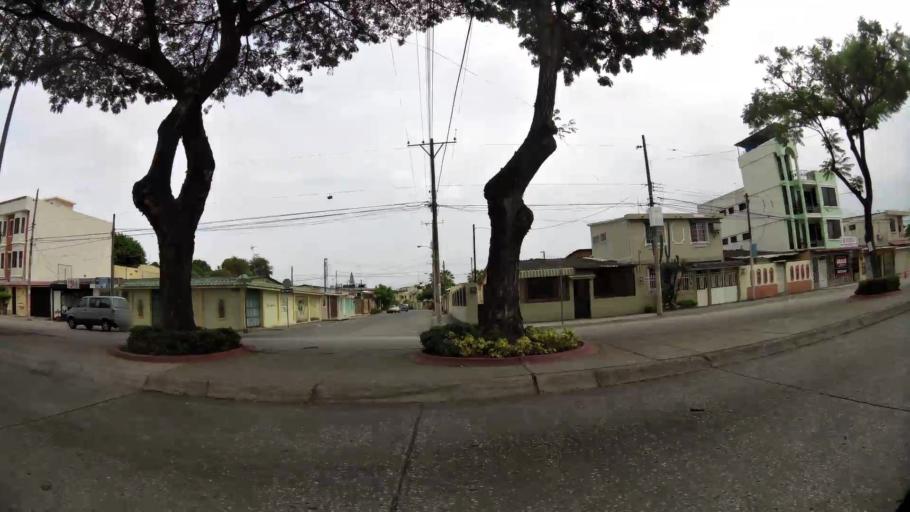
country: EC
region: Guayas
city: Eloy Alfaro
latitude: -2.1213
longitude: -79.8971
